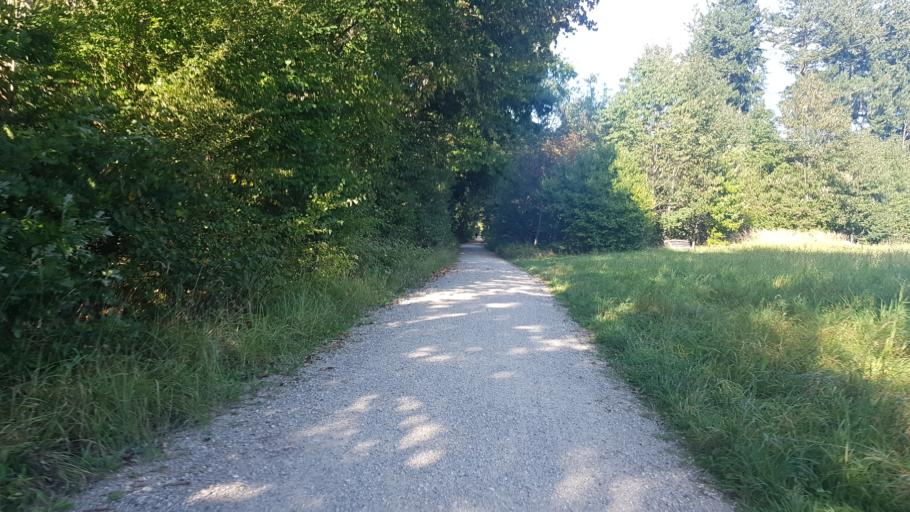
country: DE
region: Bavaria
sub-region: Upper Bavaria
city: Krailling
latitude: 48.0964
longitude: 11.3913
